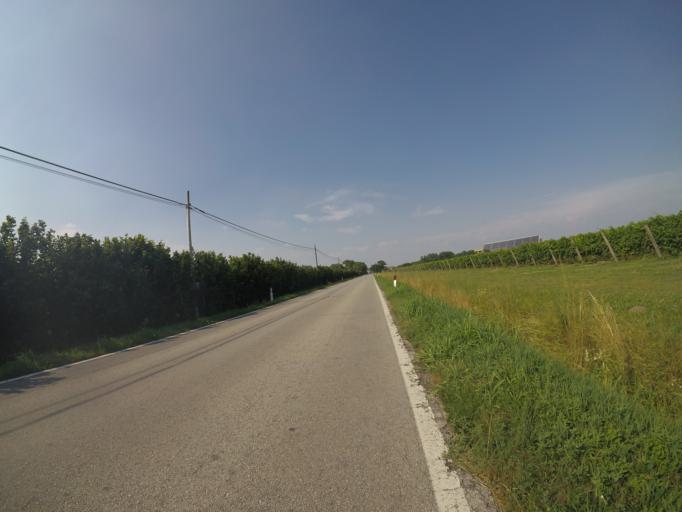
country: IT
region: Friuli Venezia Giulia
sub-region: Provincia di Udine
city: Camino al Tagliamento
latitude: 45.9364
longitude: 12.9604
